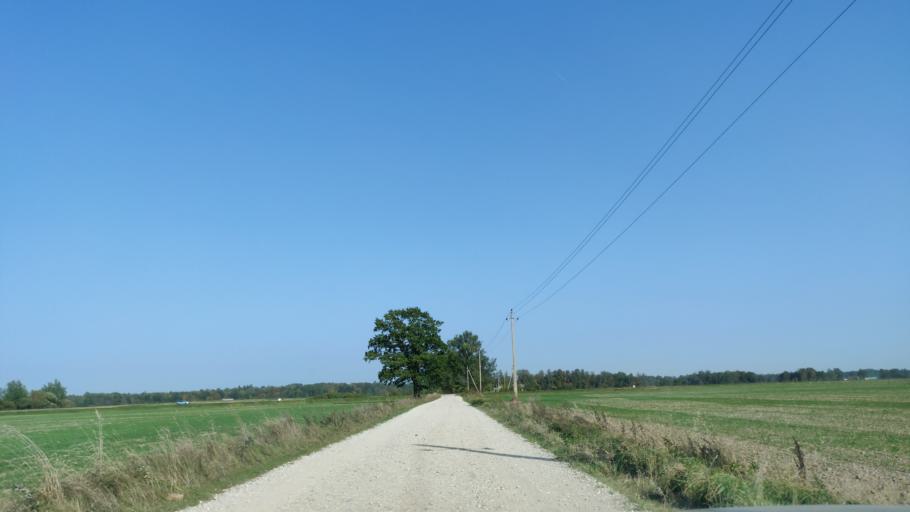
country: LT
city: Sirvintos
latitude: 54.9720
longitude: 24.8126
